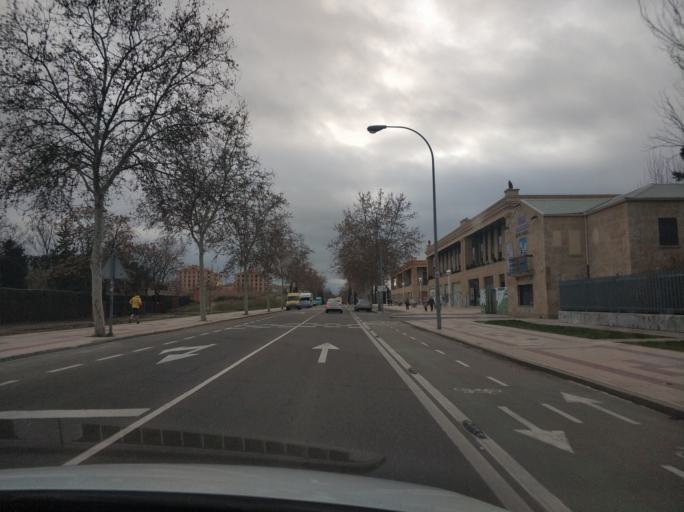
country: ES
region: Castille and Leon
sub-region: Provincia de Salamanca
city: Salamanca
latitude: 40.9814
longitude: -5.6552
